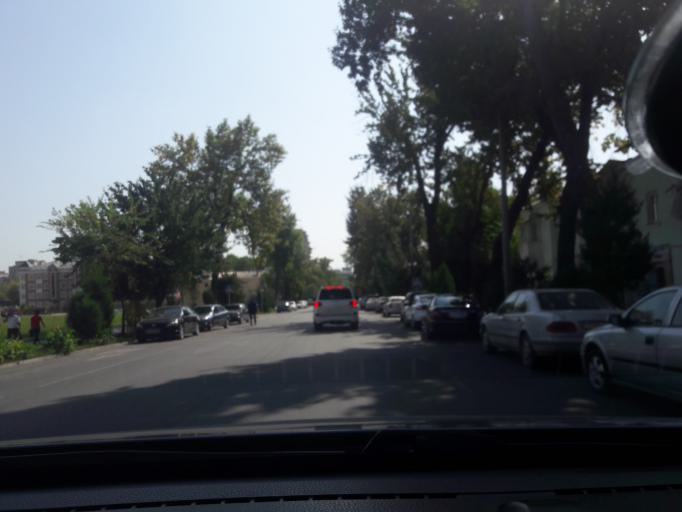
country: TJ
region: Dushanbe
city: Dushanbe
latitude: 38.5673
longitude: 68.7998
